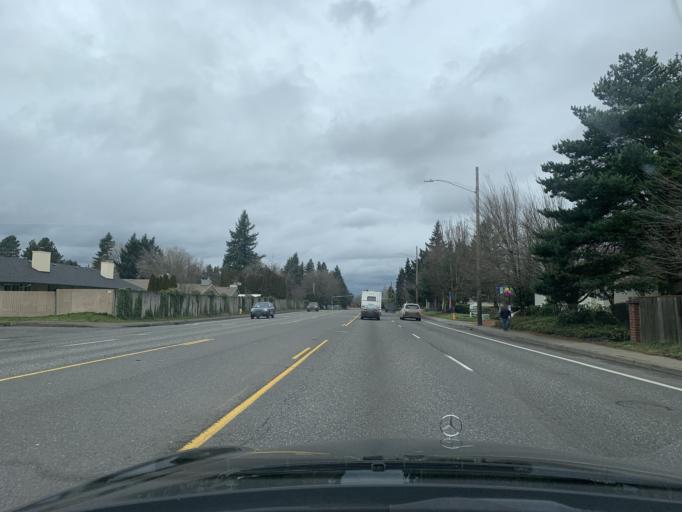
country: US
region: Oregon
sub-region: Multnomah County
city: Troutdale
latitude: 45.5241
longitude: -122.3984
